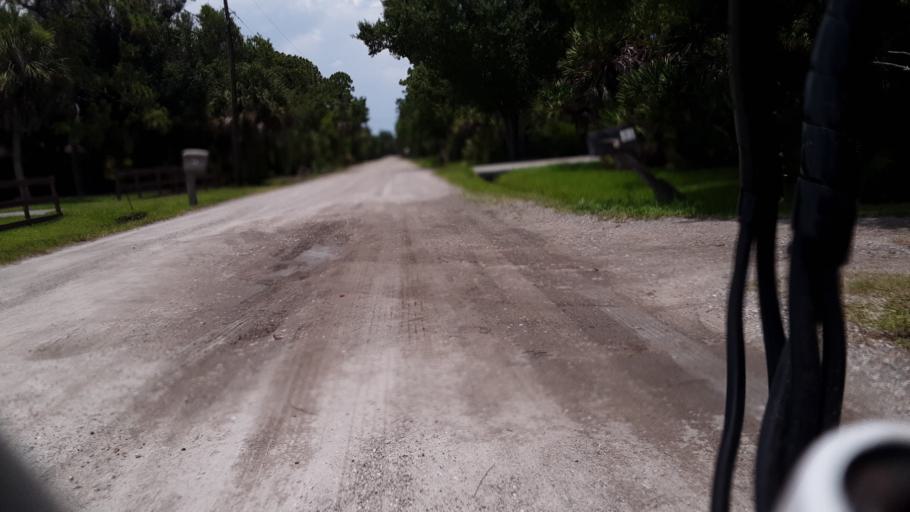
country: US
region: Florida
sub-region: Brevard County
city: Malabar
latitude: 27.9883
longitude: -80.6018
